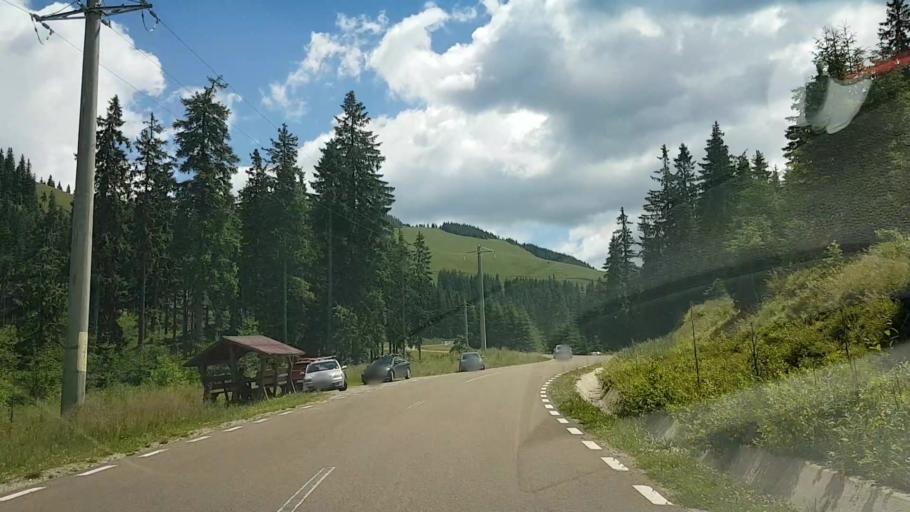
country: RO
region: Suceava
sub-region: Comuna Sadova
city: Sadova
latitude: 47.4581
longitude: 25.5199
